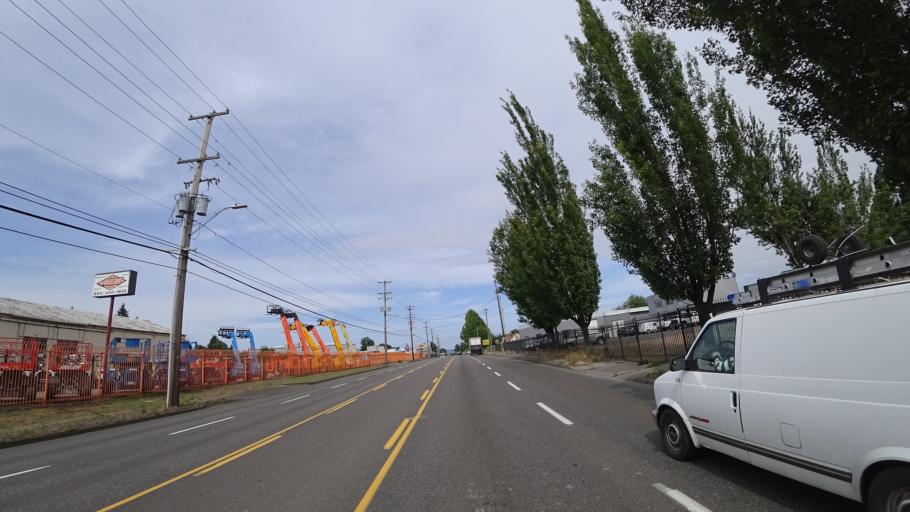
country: US
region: Oregon
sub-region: Multnomah County
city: Portland
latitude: 45.5720
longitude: -122.6219
